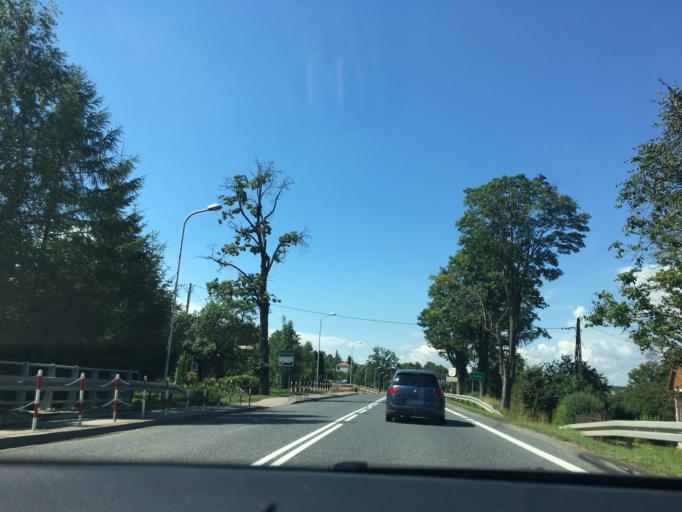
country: PL
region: Subcarpathian Voivodeship
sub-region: Powiat krosnienski
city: Dukla
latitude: 49.5427
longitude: 21.6911
